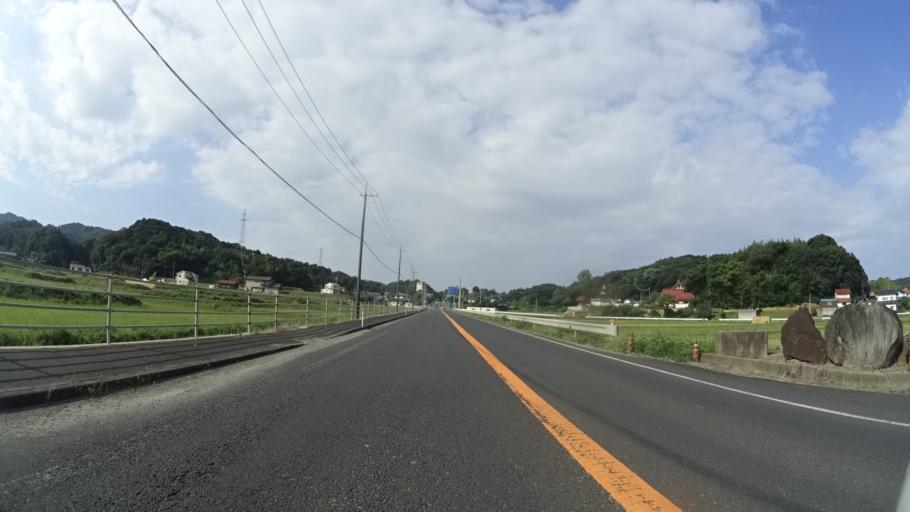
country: JP
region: Shimane
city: Odacho-oda
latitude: 35.2425
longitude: 132.5411
